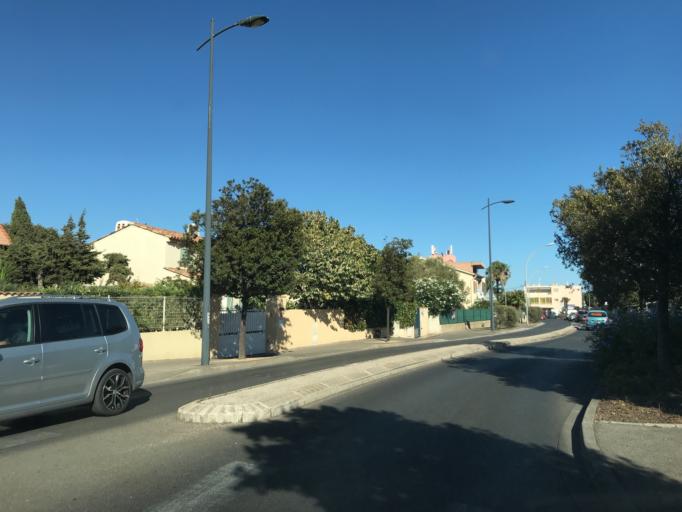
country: FR
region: Provence-Alpes-Cote d'Azur
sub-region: Departement du Var
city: La Seyne-sur-Mer
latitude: 43.0829
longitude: 5.8772
